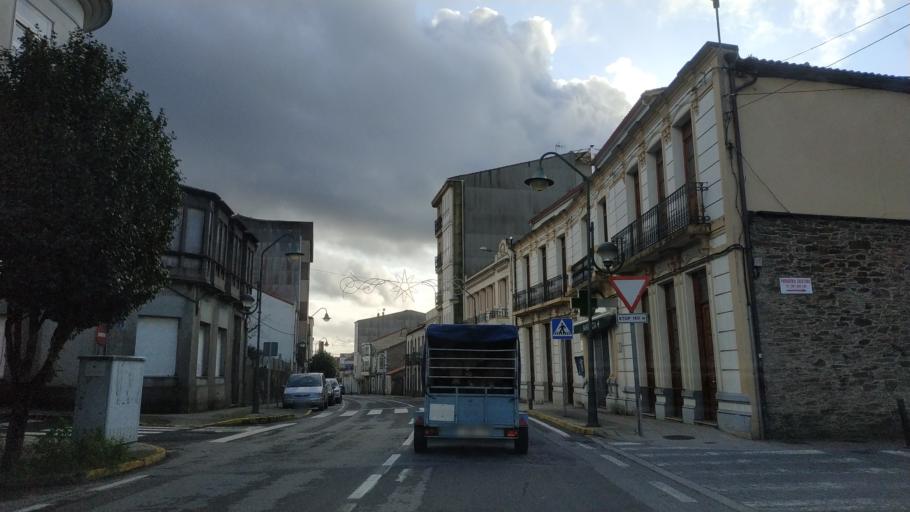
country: ES
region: Galicia
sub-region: Provincia da Coruna
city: Arzua
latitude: 42.9286
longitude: -8.1638
